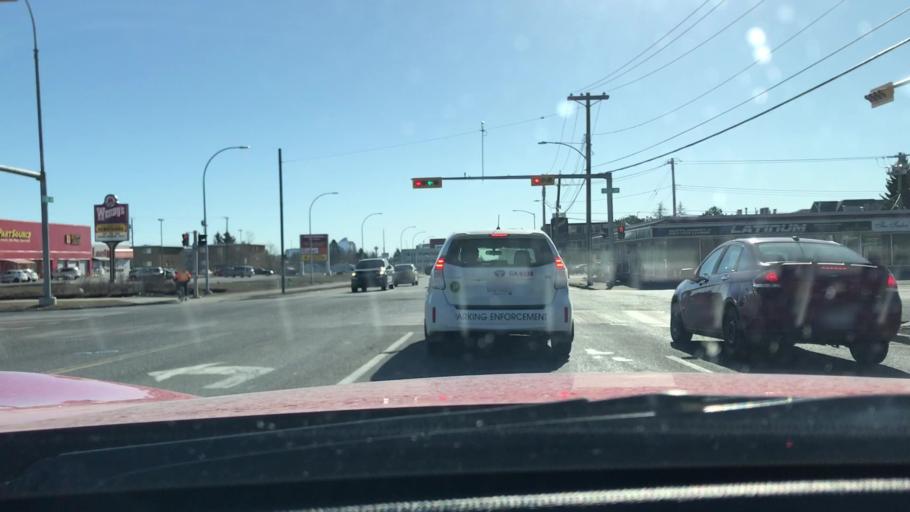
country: CA
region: Alberta
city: Calgary
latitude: 51.0378
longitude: -114.1416
